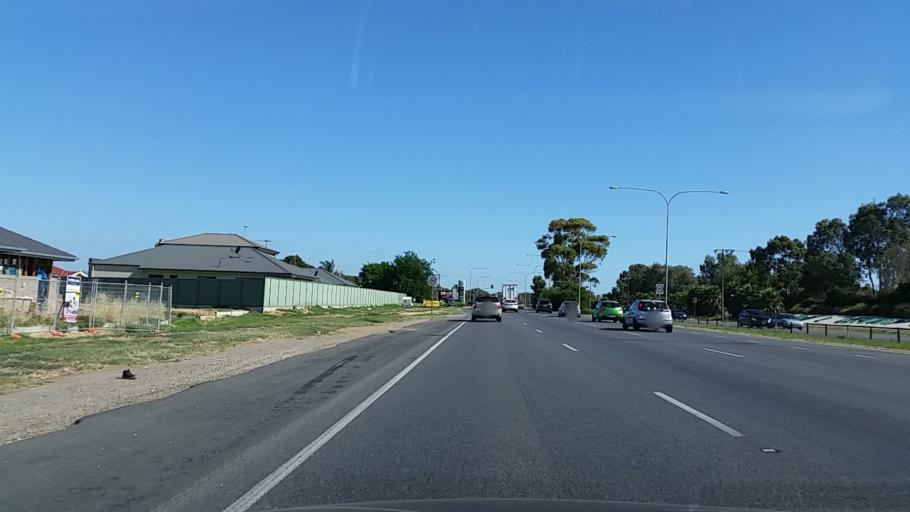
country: AU
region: South Australia
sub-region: Salisbury
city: Salisbury
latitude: -34.7607
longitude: 138.5922
